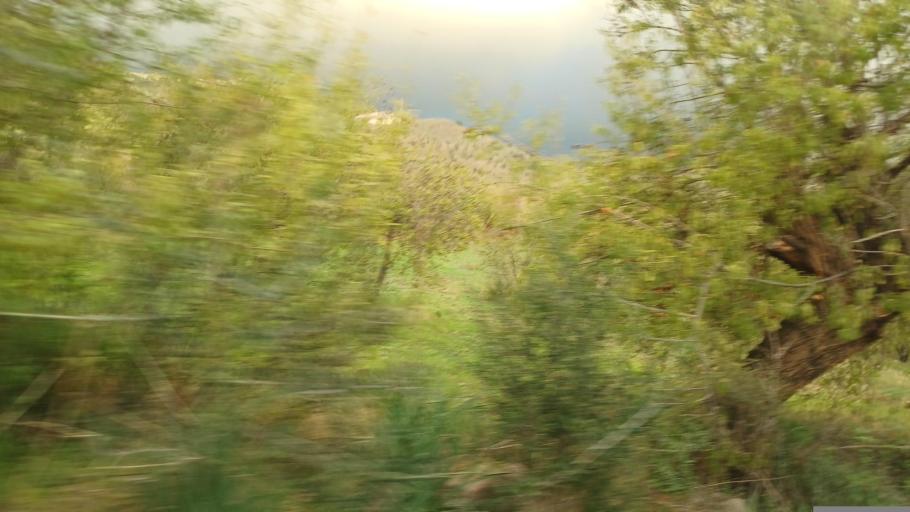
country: CY
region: Pafos
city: Mesogi
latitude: 34.7869
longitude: 32.5210
